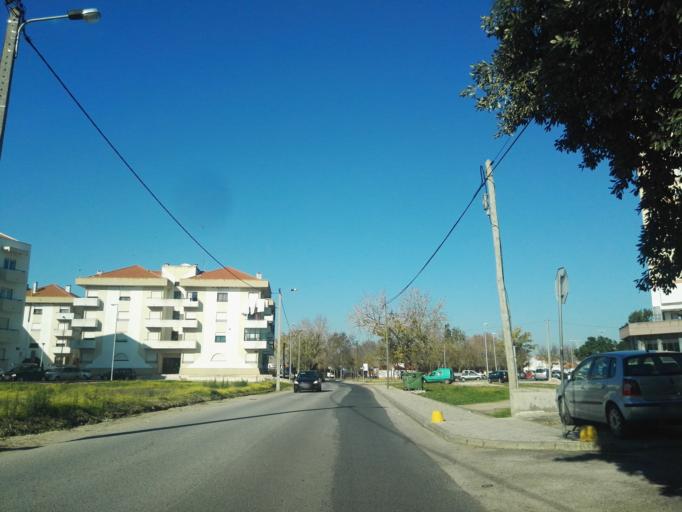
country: PT
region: Santarem
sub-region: Benavente
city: Samora Correia
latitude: 38.9349
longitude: -8.8655
